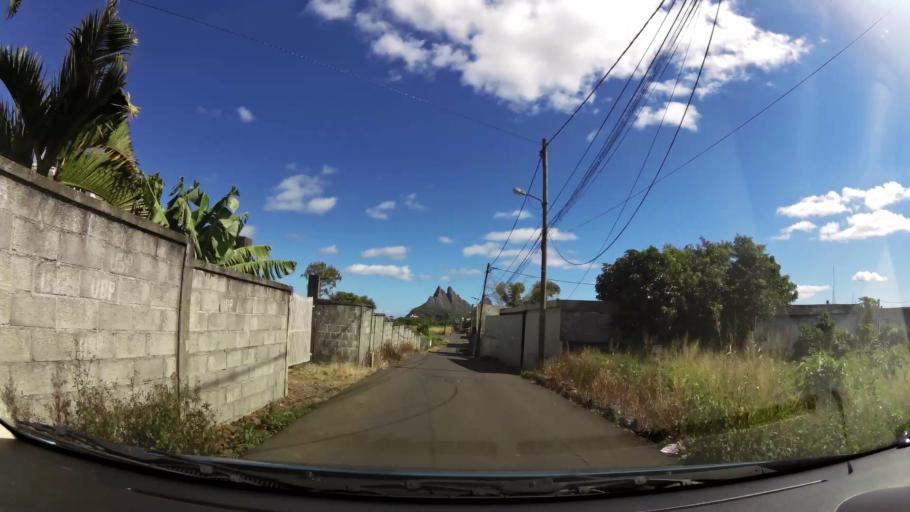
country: MU
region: Plaines Wilhems
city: Vacoas
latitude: -20.3066
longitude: 57.4789
